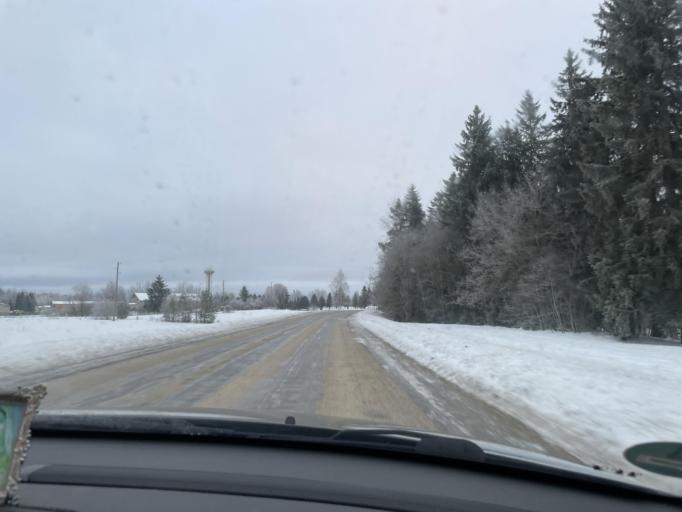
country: LV
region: Rezekne
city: Rezekne
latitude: 56.4950
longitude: 27.4229
